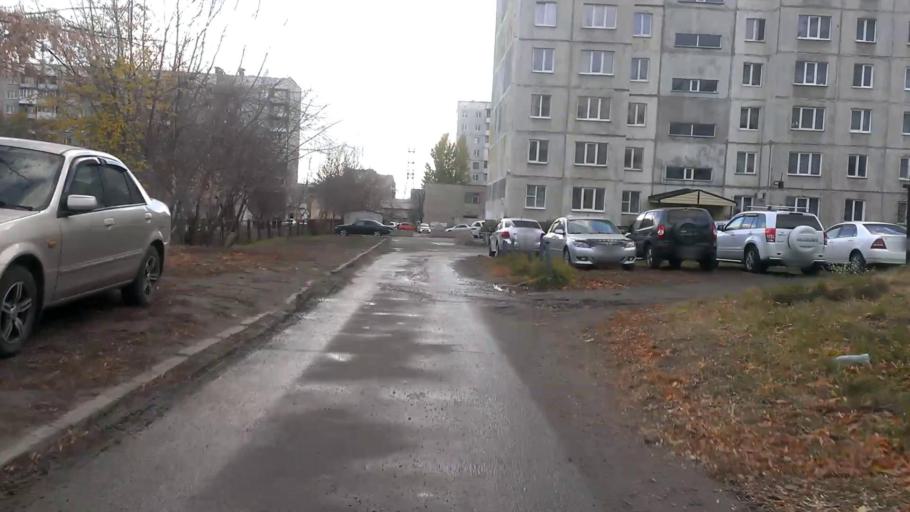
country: RU
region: Altai Krai
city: Novosilikatnyy
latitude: 53.3579
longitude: 83.6761
